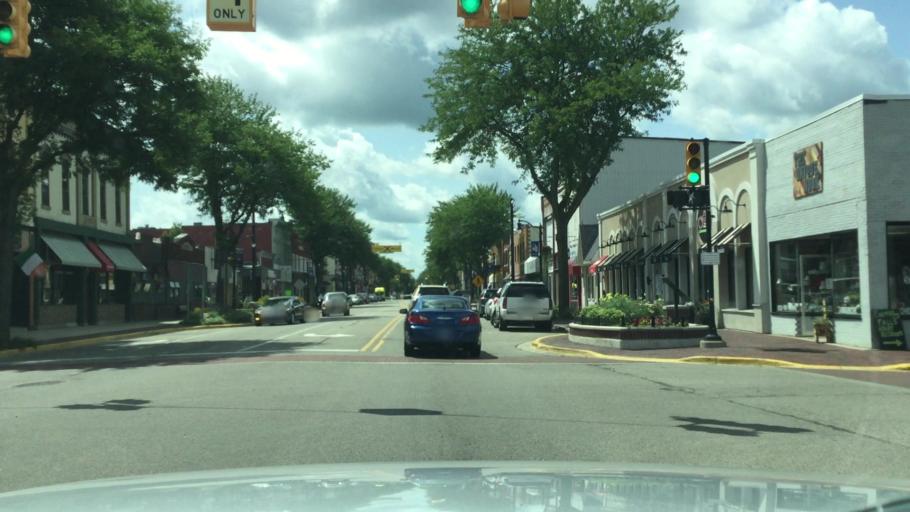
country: US
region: Michigan
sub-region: Montcalm County
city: Greenville
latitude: 43.1808
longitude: -85.2532
